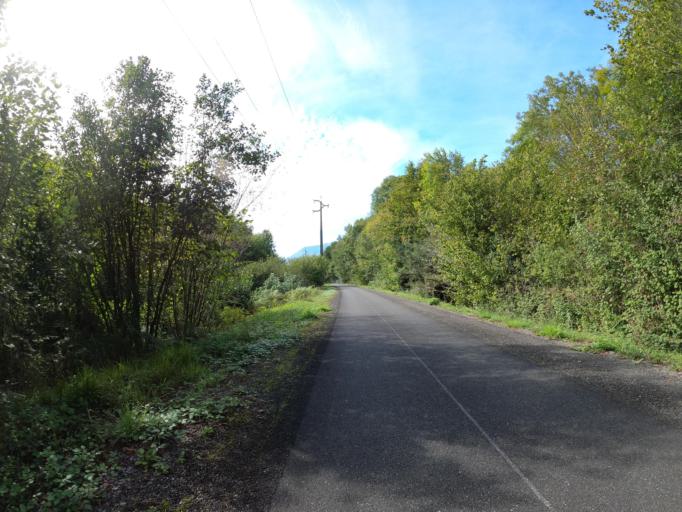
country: FR
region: Midi-Pyrenees
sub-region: Departement des Hautes-Pyrenees
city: Argeles-Gazost
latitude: 43.0409
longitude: -0.0594
